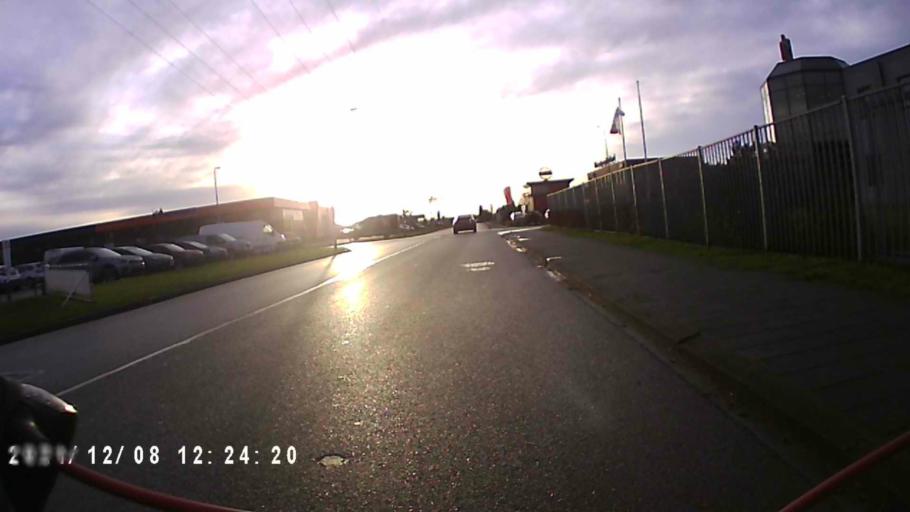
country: NL
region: Groningen
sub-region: Gemeente Groningen
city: Oosterpark
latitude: 53.2218
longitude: 6.6106
